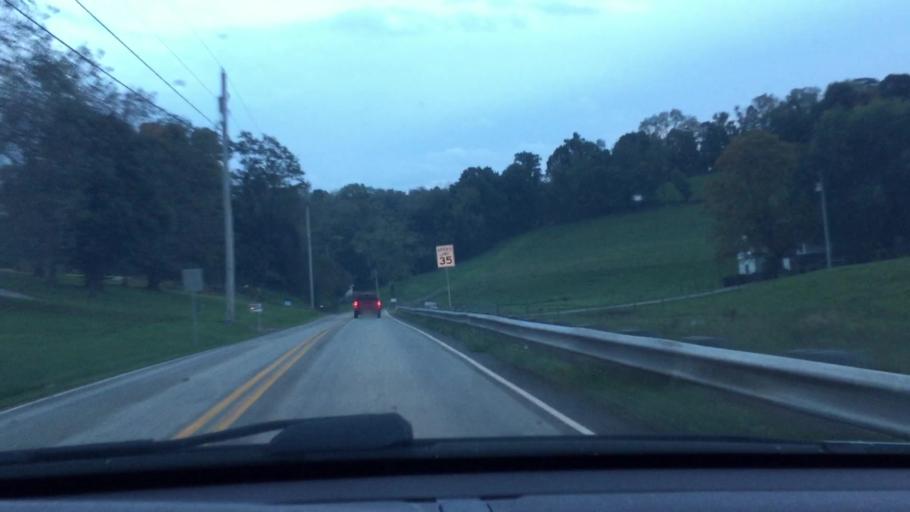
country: US
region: Pennsylvania
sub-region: Washington County
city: McGovern
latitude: 40.1905
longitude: -80.1934
